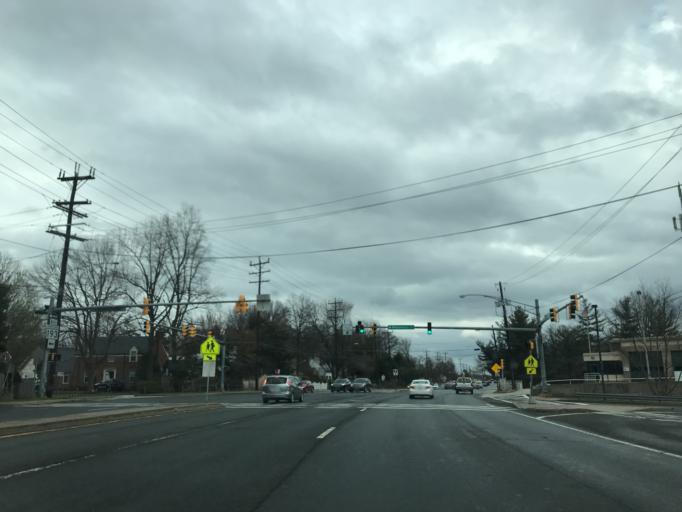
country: US
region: Maryland
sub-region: Montgomery County
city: Four Corners
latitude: 39.0184
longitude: -77.0076
